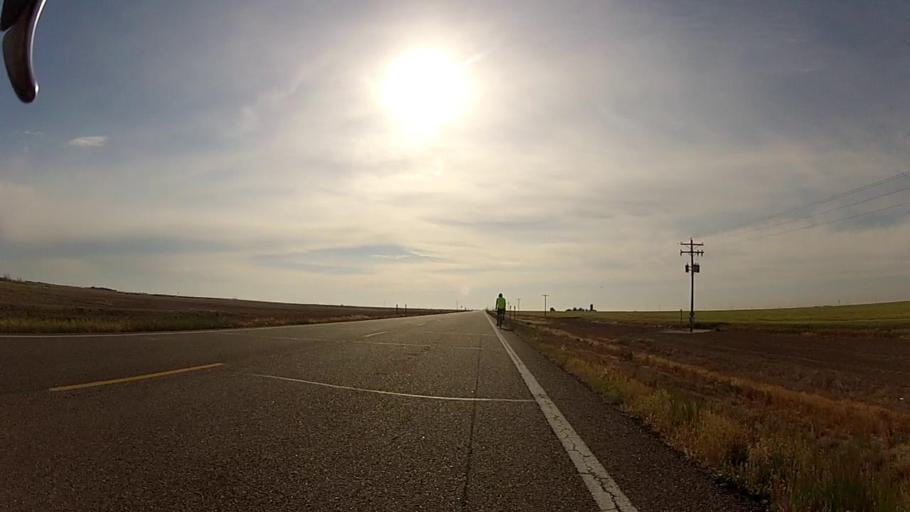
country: US
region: Kansas
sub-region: Grant County
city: Ulysses
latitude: 37.5766
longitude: -101.4585
